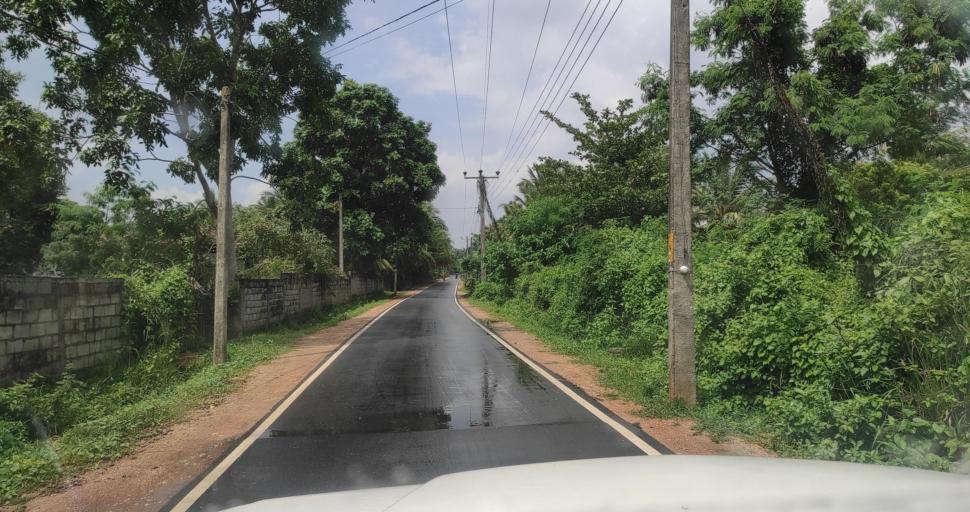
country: LK
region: Eastern Province
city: Trincomalee
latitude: 8.3735
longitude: 81.0106
